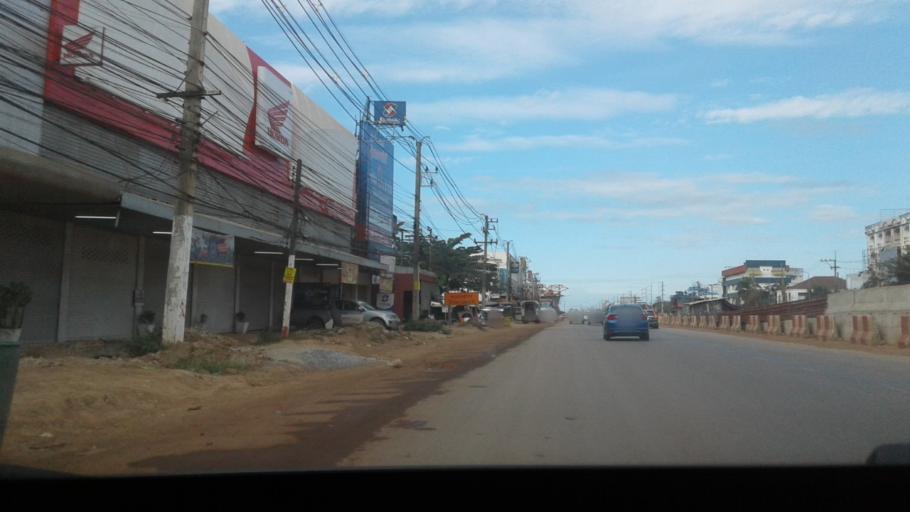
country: TH
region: Changwat Udon Thani
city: Udon Thani
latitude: 17.4321
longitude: 102.7913
